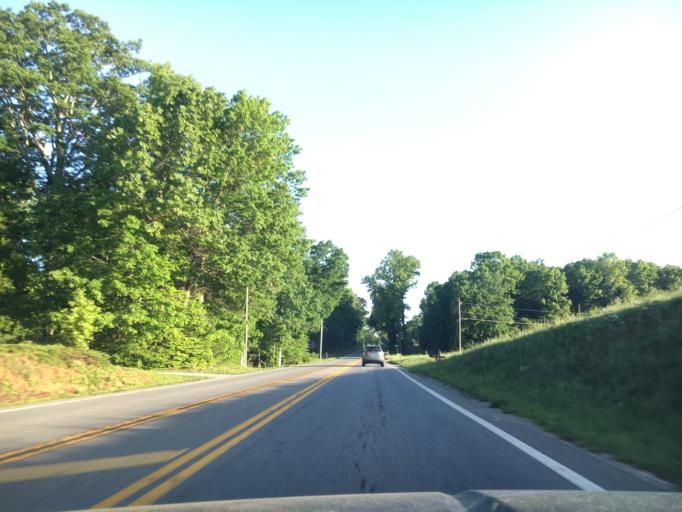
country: US
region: Virginia
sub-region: Campbell County
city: Rustburg
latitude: 37.2518
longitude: -79.1190
